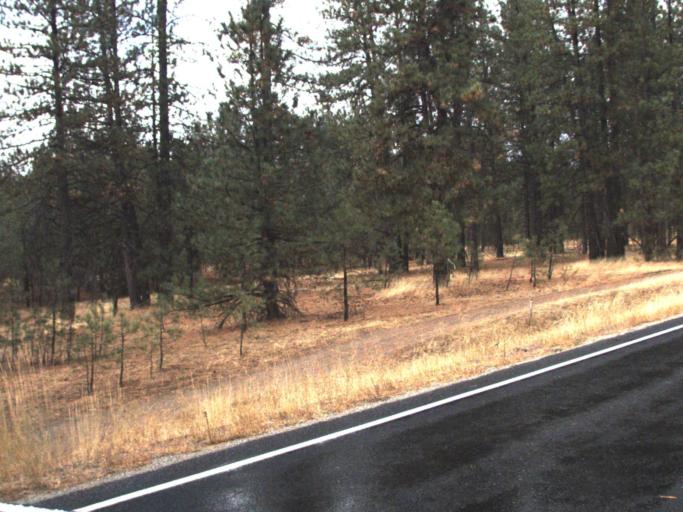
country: US
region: Washington
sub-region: Spokane County
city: Deer Park
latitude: 48.0045
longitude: -117.7278
